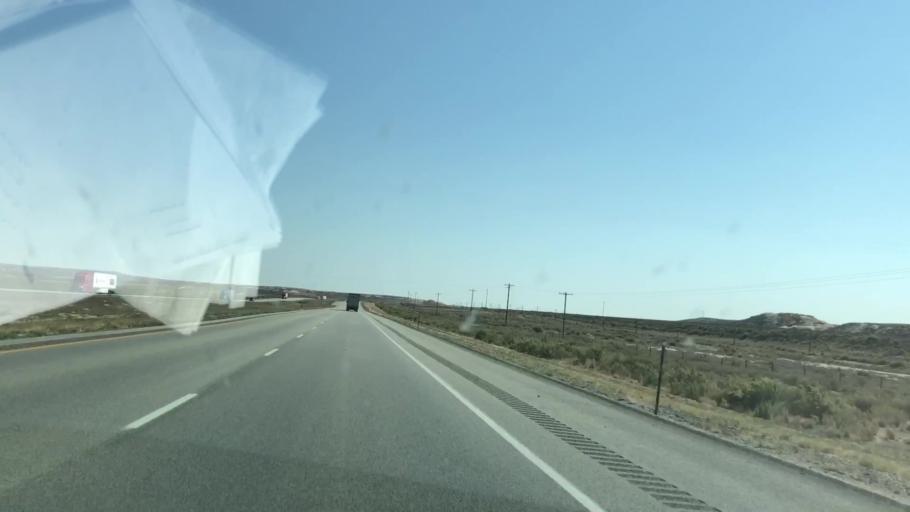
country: US
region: Wyoming
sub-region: Carbon County
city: Rawlins
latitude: 41.6999
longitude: -107.9084
